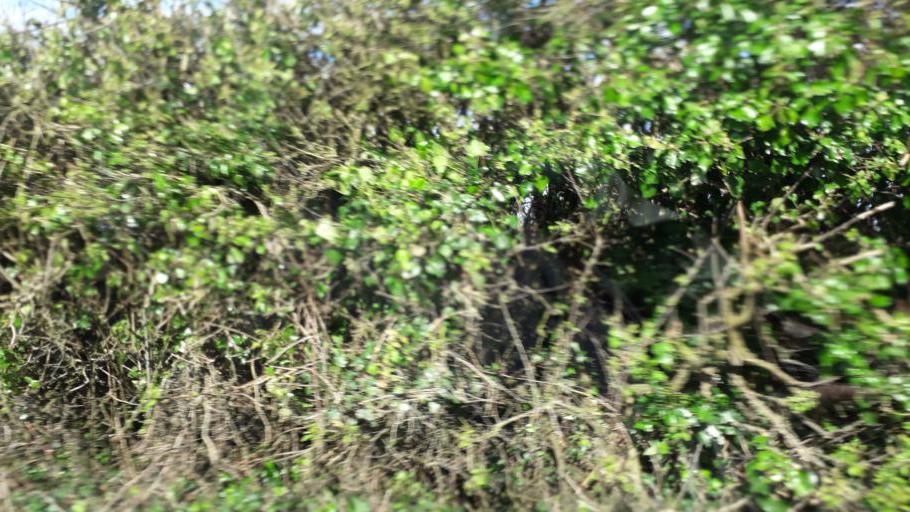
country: IE
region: Leinster
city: Ballymun
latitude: 53.4491
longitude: -6.2761
